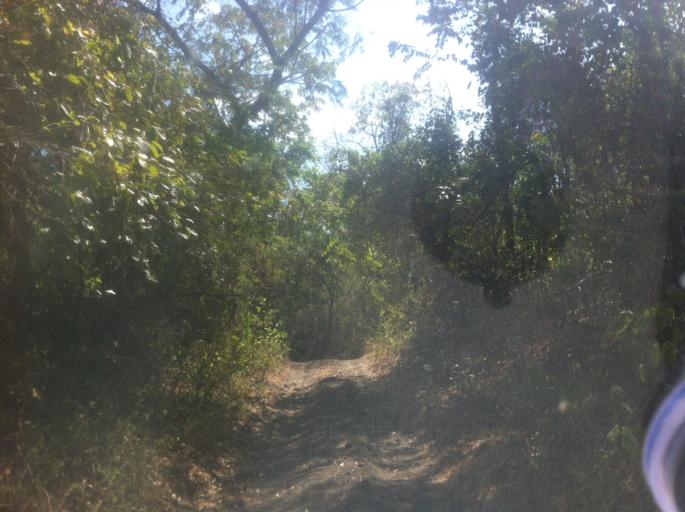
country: NI
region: Chinandega
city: Chichigalpa
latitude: 12.6917
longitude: -87.0279
